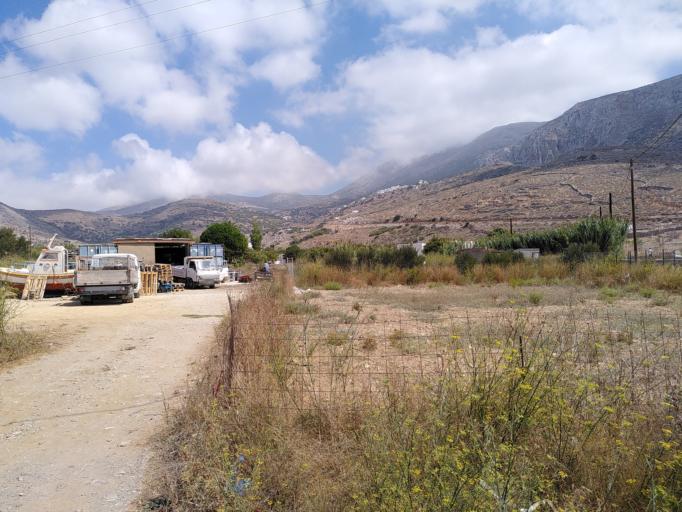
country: GR
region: South Aegean
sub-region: Nomos Kykladon
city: Amorgos
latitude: 36.9056
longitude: 25.9793
